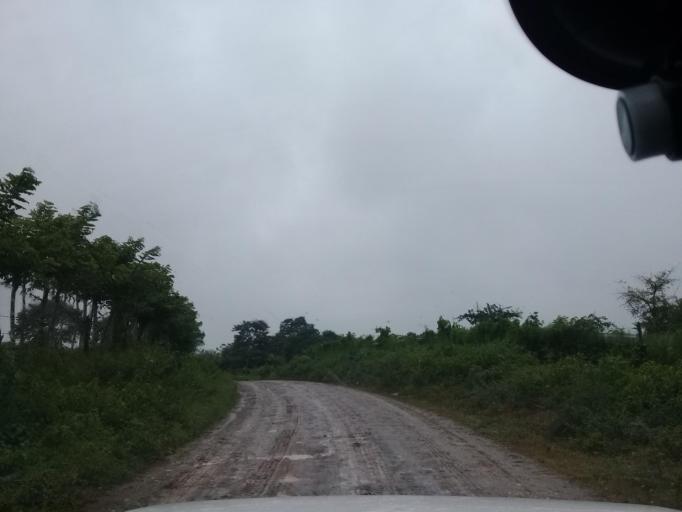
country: MX
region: Veracruz
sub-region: Chalma
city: San Pedro Coyutla
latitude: 21.2437
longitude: -98.4615
